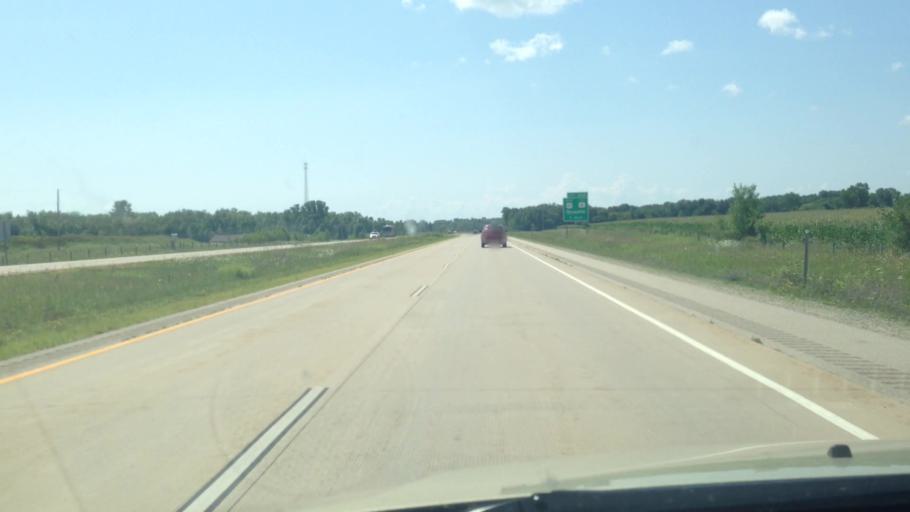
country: US
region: Wisconsin
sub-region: Oconto County
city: Oconto
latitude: 44.9396
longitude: -87.8707
